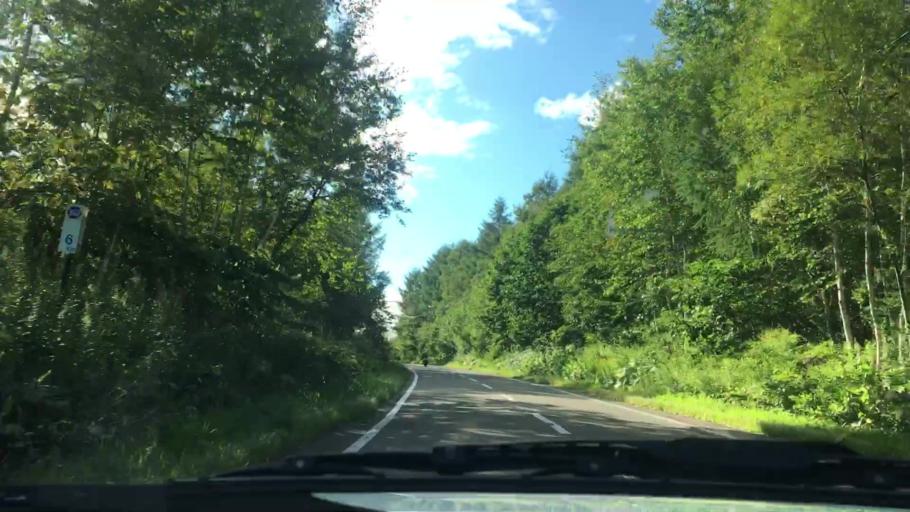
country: JP
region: Hokkaido
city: Otofuke
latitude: 43.1726
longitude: 142.9727
